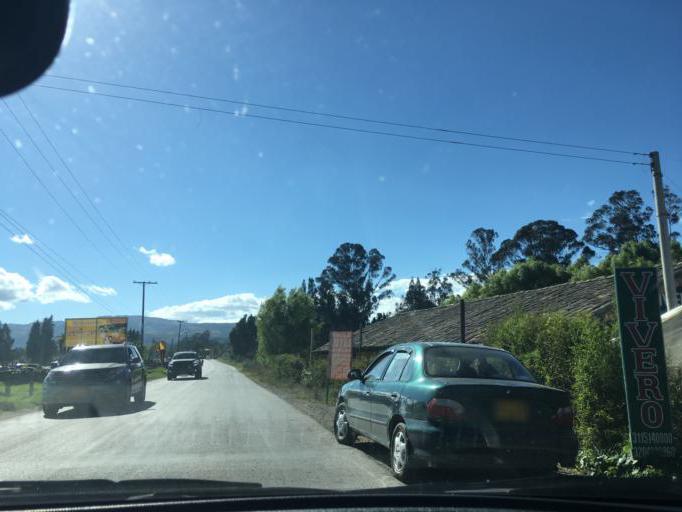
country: CO
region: Boyaca
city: Firavitoba
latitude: 5.6655
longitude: -72.9683
